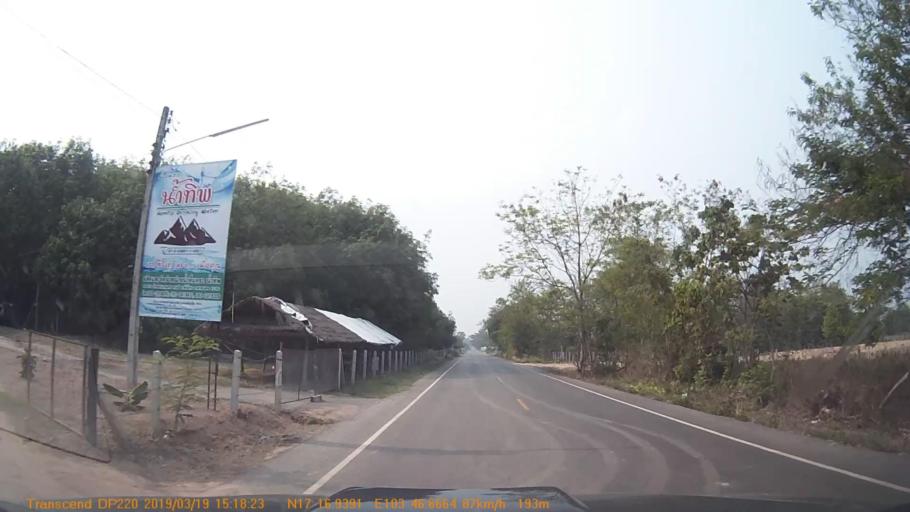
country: TH
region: Sakon Nakhon
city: Phanna Nikhom
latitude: 17.2827
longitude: 103.7776
